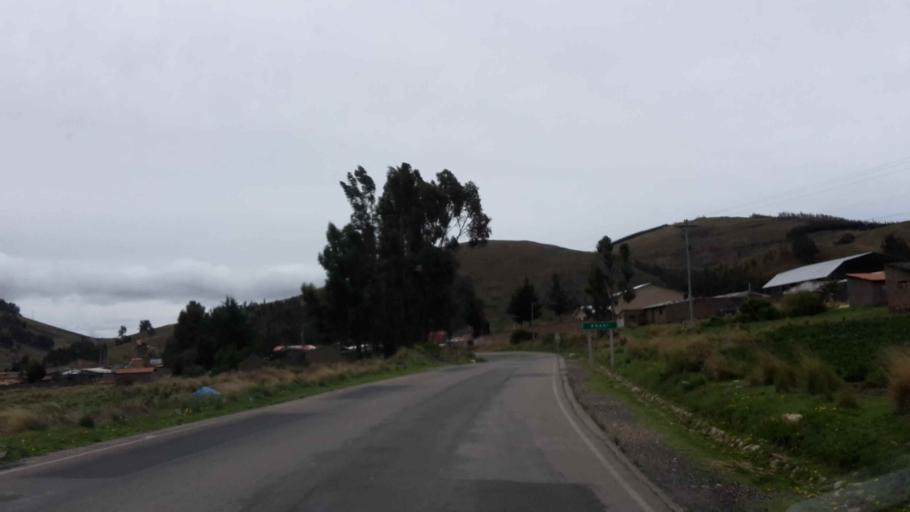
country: BO
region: Cochabamba
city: Arani
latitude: -17.4807
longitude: -65.5747
